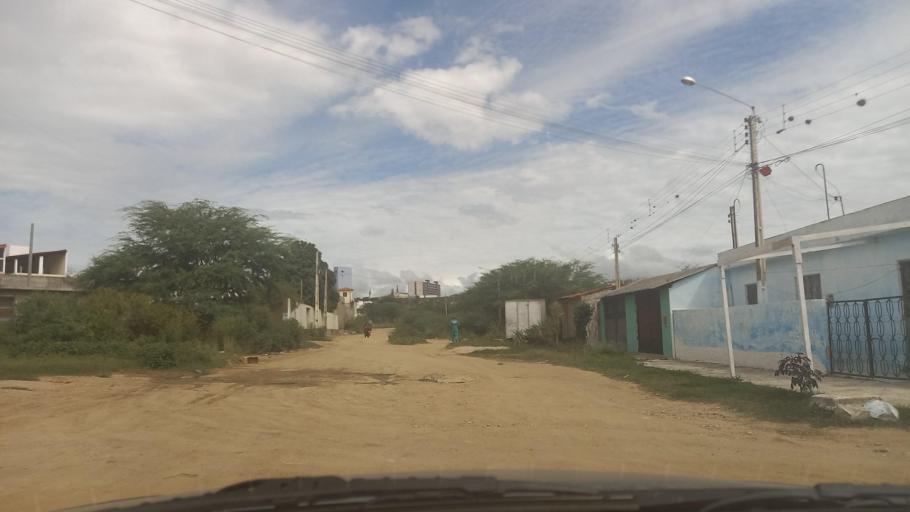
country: BR
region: Pernambuco
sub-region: Caruaru
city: Caruaru
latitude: -8.2930
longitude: -35.9920
